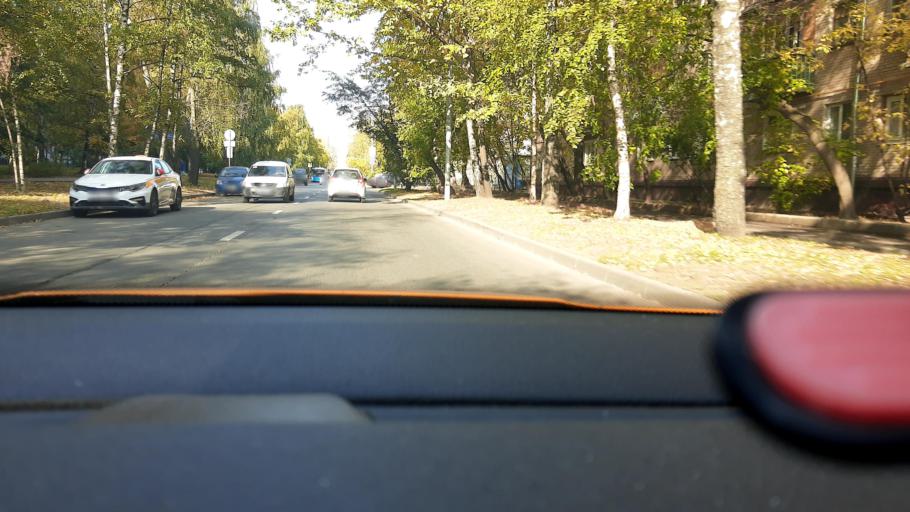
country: RU
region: Moscow
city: Vagonoremont
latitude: 55.8939
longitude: 37.5297
